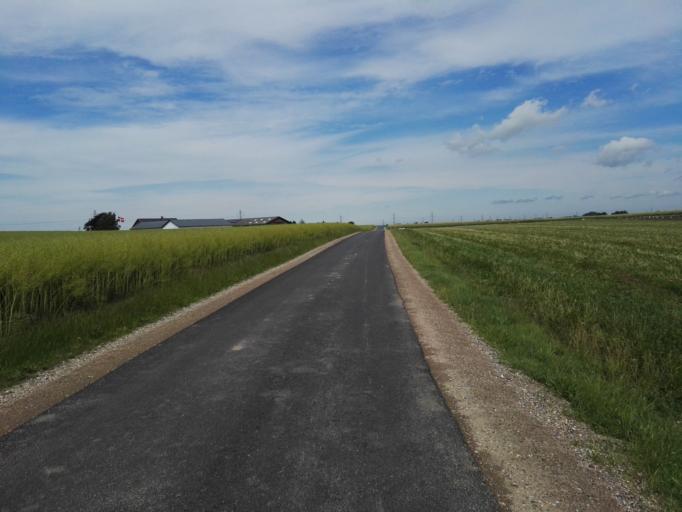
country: DK
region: Capital Region
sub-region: Egedal Kommune
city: Olstykke
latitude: 55.8180
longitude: 12.1708
